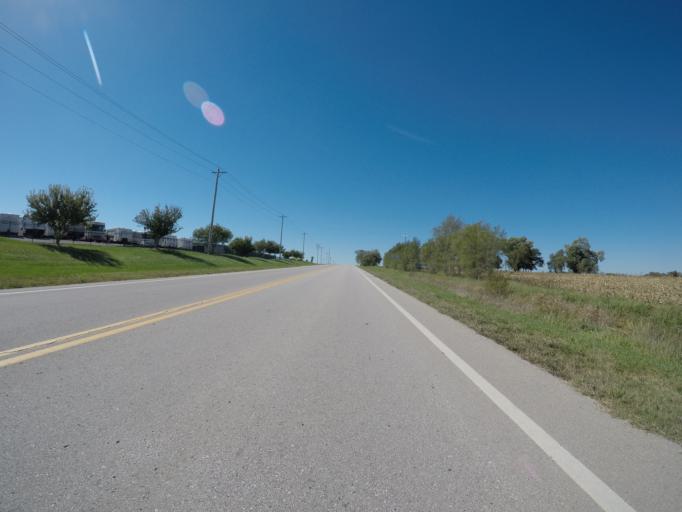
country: US
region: Kansas
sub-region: Douglas County
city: Eudora
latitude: 38.9424
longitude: -95.0780
